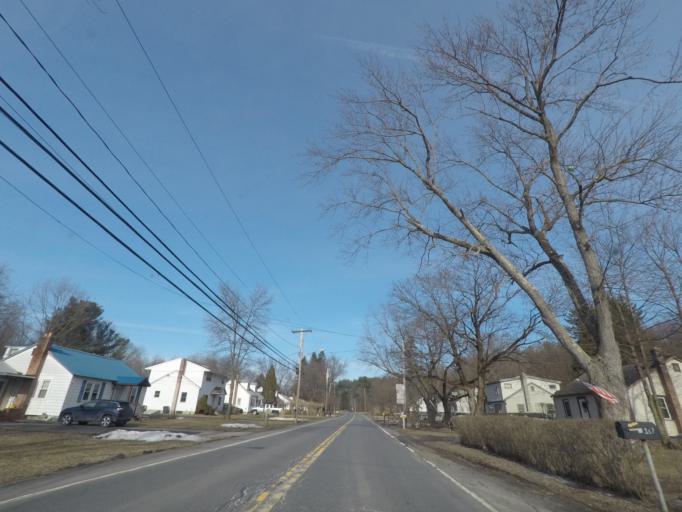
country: US
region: New York
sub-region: Rensselaer County
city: Nassau
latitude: 42.5042
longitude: -73.6158
